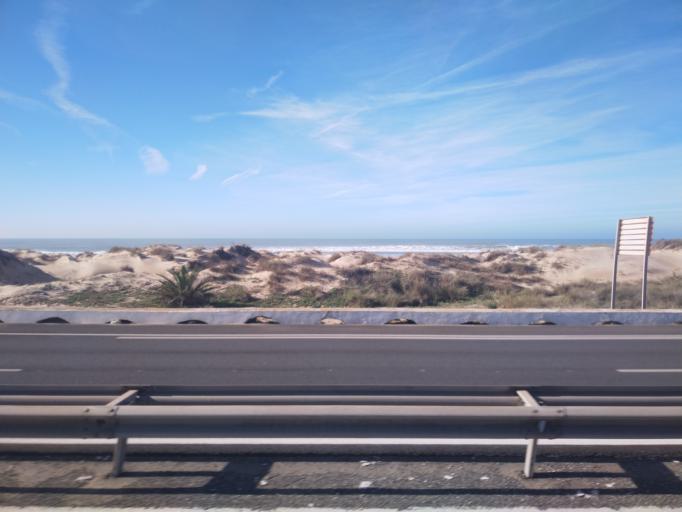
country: ES
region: Andalusia
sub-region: Provincia de Cadiz
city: San Fernando
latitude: 36.4755
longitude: -6.2593
